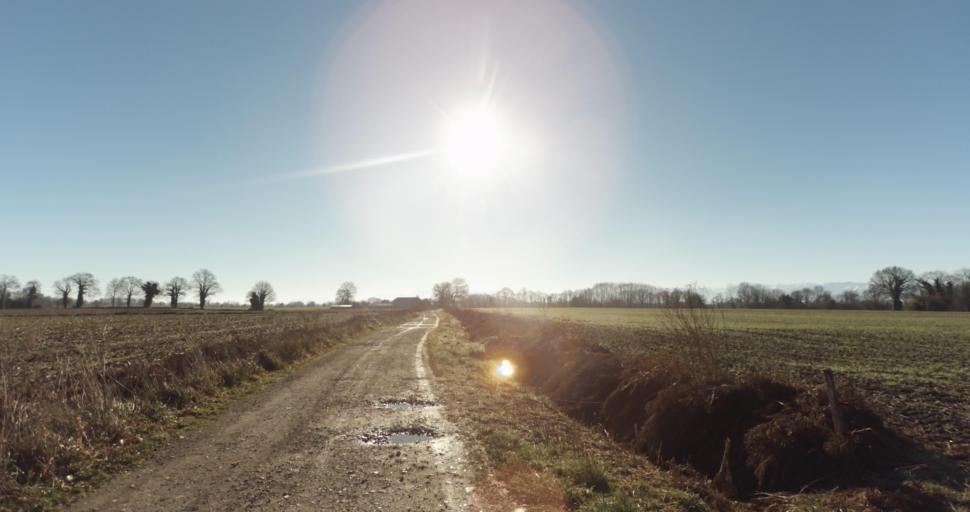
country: FR
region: Aquitaine
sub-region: Departement des Pyrenees-Atlantiques
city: Morlaas
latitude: 43.3440
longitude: -0.2388
